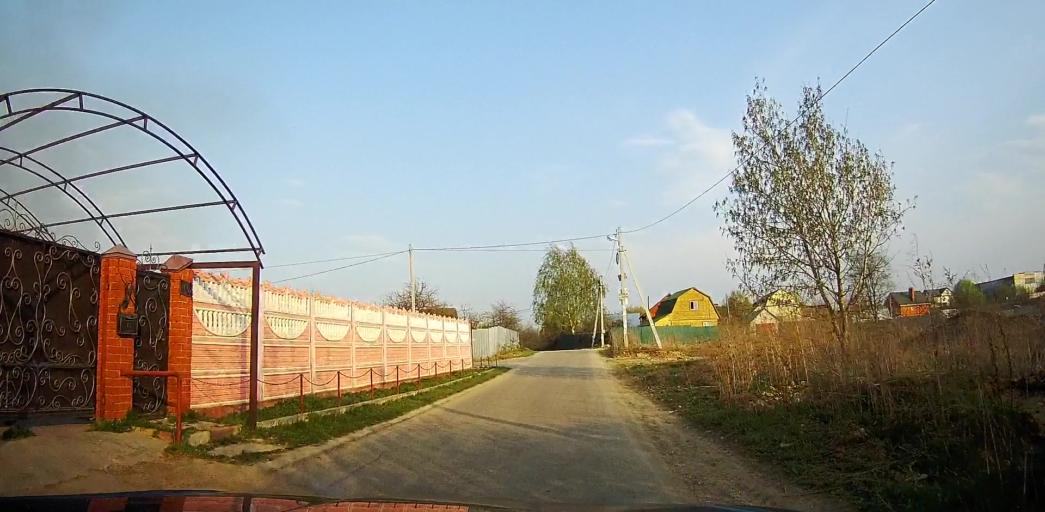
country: RU
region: Moskovskaya
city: Andreyevskoye
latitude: 55.5439
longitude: 37.9735
